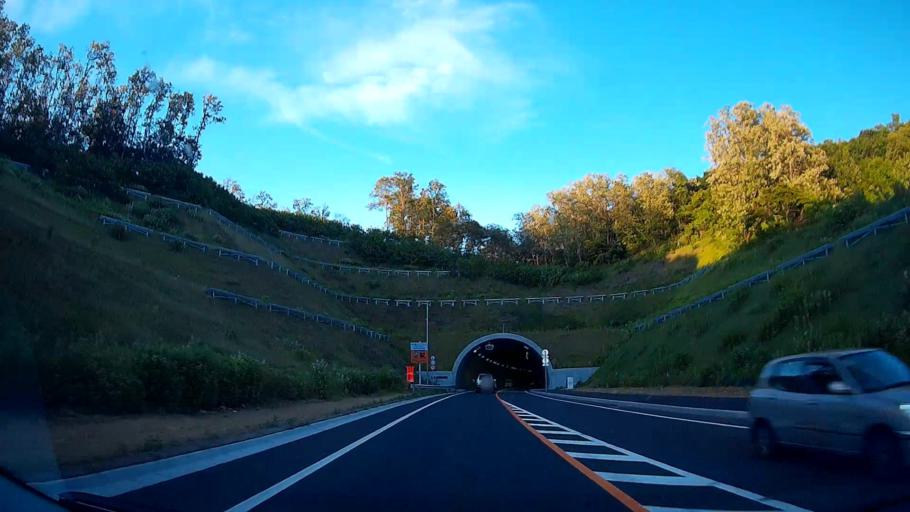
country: JP
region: Hokkaido
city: Yoichi
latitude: 43.2035
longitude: 140.8730
